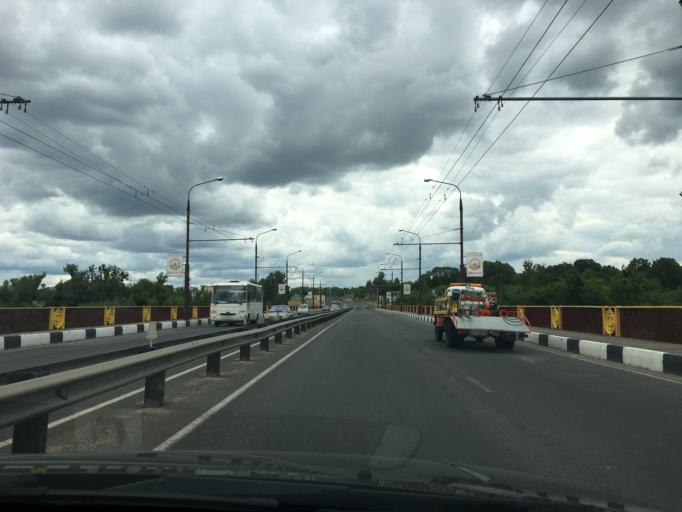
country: BY
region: Grodnenskaya
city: Hrodna
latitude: 53.6602
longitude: 23.8593
